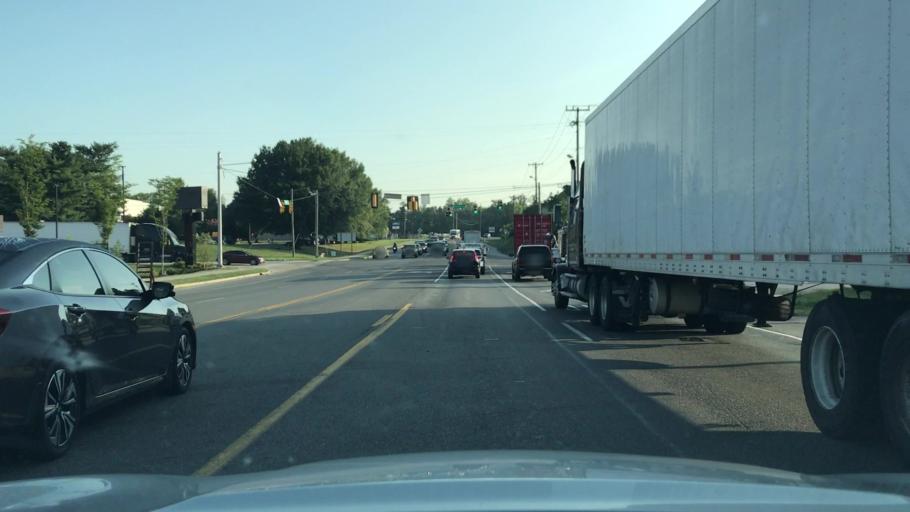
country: US
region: Tennessee
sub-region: Rutherford County
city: La Vergne
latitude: 36.0161
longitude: -86.6200
